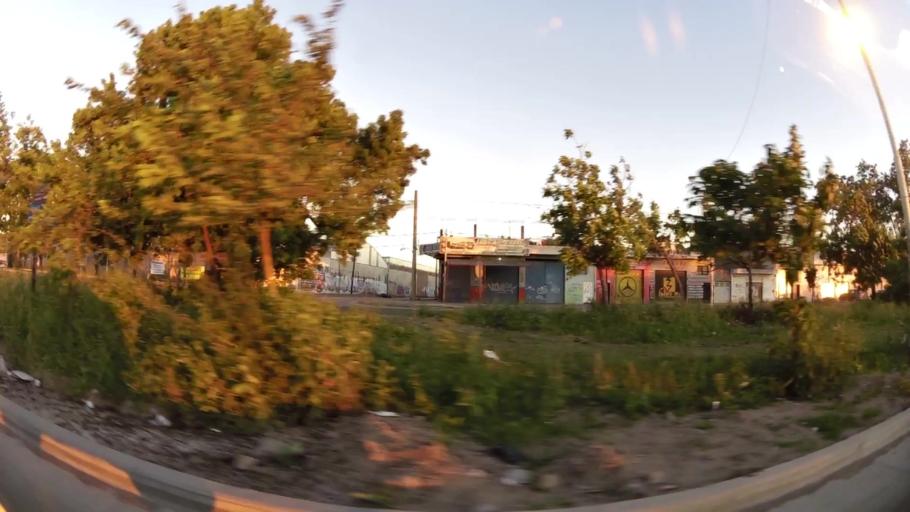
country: AR
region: Buenos Aires
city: Pontevedra
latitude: -34.7434
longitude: -58.6077
